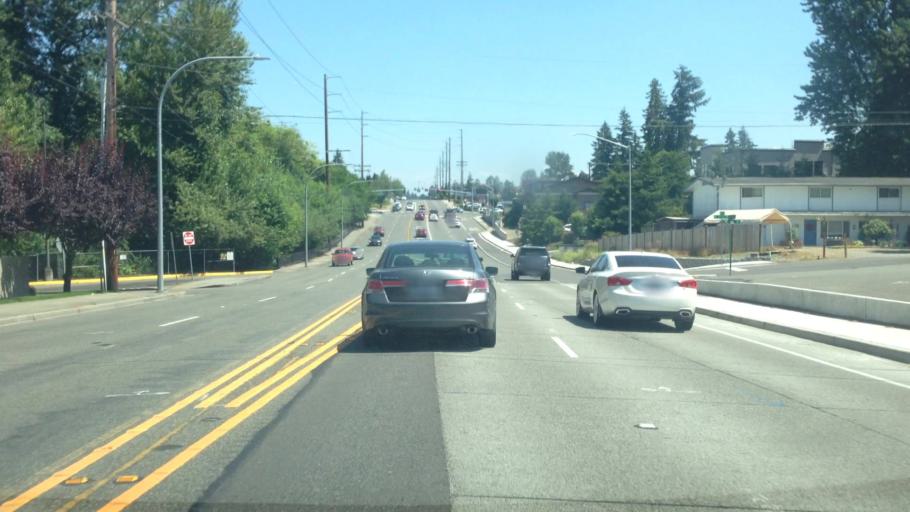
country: US
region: Washington
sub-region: Pierce County
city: Puyallup
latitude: 47.1548
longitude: -122.3074
